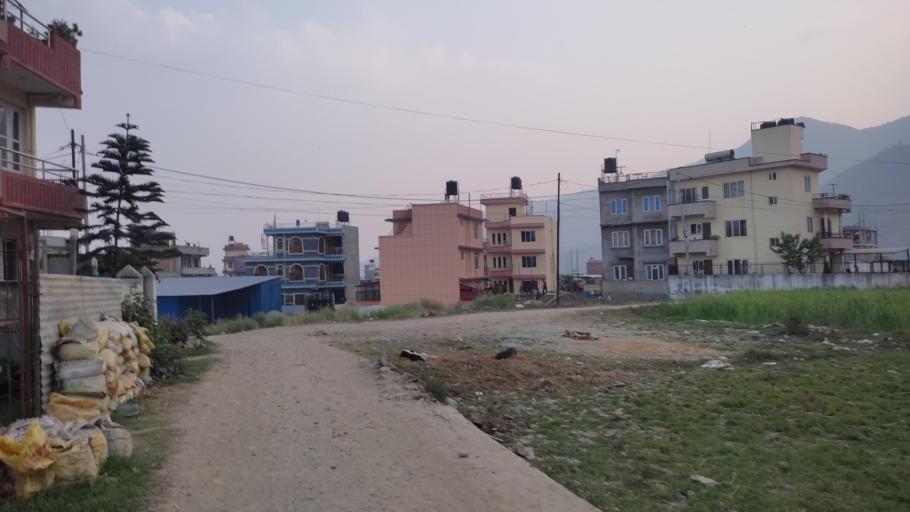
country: NP
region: Central Region
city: Kirtipur
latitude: 27.6658
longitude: 85.2762
